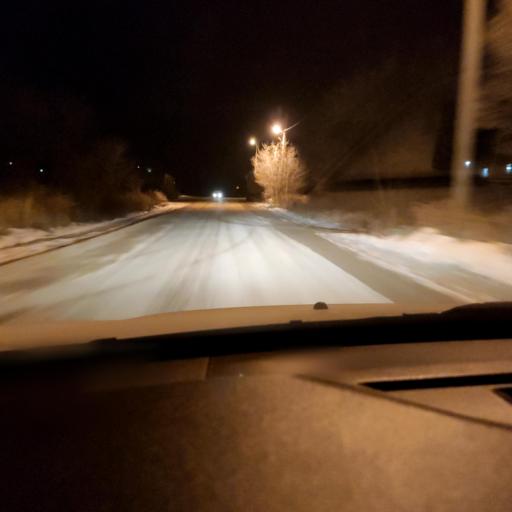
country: RU
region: Samara
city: Smyshlyayevka
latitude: 53.2387
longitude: 50.4806
